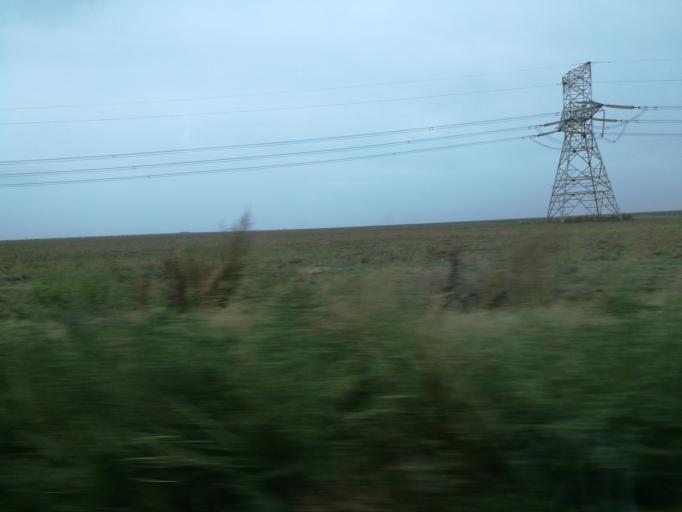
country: RO
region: Constanta
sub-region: Comuna Mihail Kogalniceanu
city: Piatra
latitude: 44.4572
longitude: 28.5562
